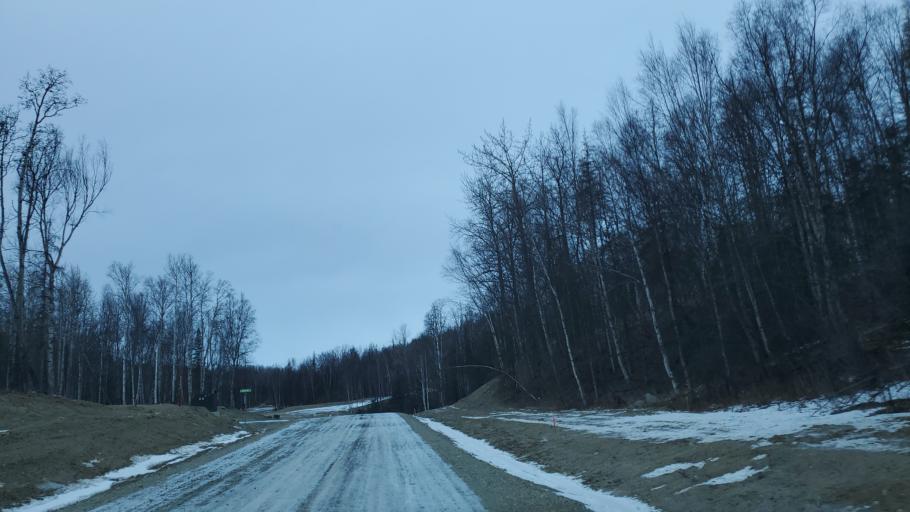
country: US
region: Alaska
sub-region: Matanuska-Susitna Borough
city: Gateway
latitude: 61.6547
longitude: -149.2296
